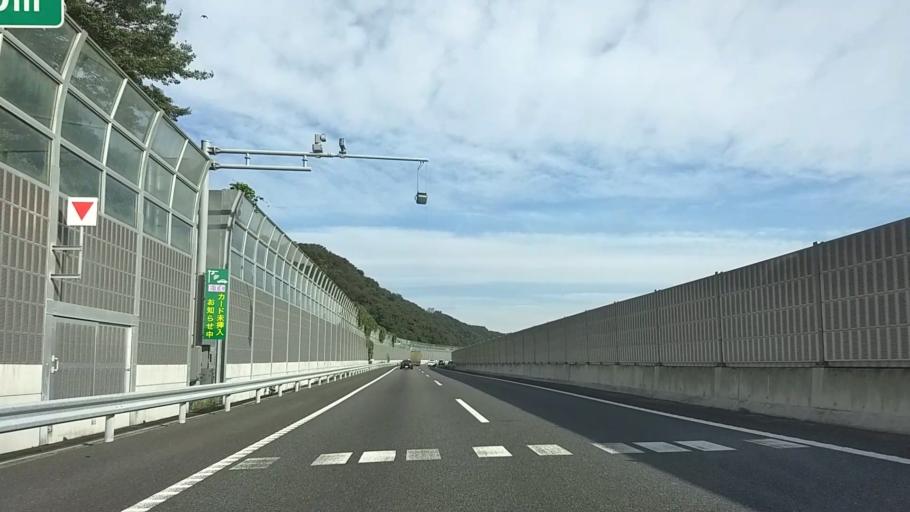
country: JP
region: Kanagawa
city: Zama
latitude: 35.4977
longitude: 139.3664
